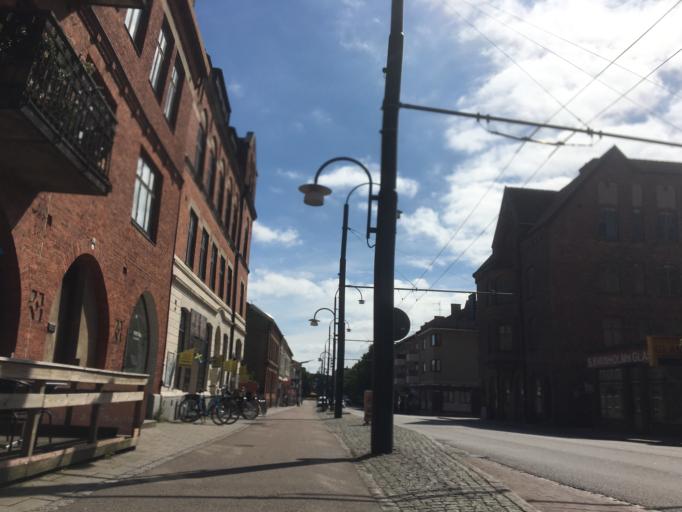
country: SE
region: Skane
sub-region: Landskrona
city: Landskrona
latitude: 55.8783
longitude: 12.8341
